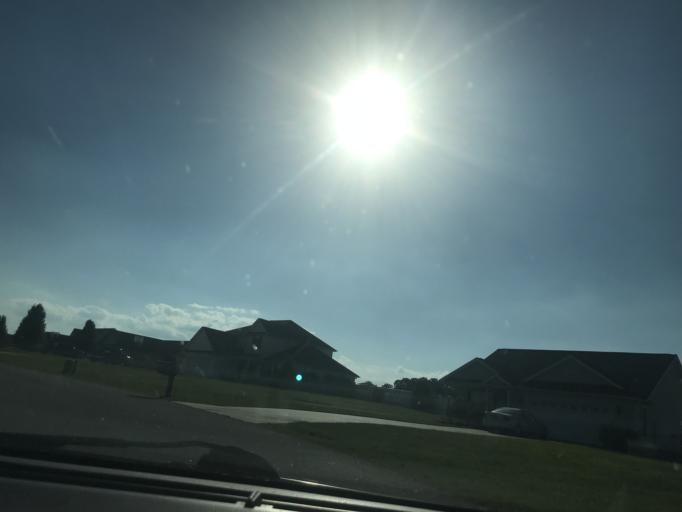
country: US
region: North Carolina
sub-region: Cleveland County
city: Boiling Springs
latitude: 35.1718
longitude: -81.7159
